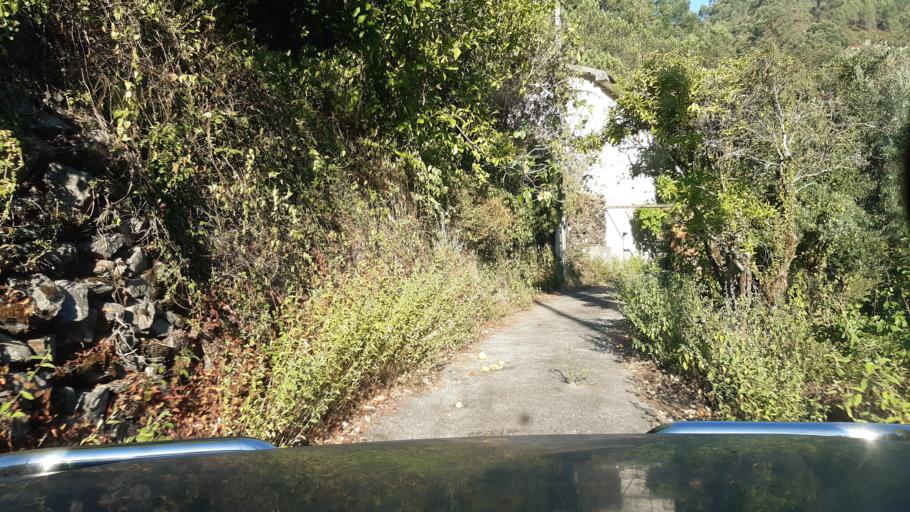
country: PT
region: Viseu
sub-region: Mortagua
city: Mortagua
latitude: 40.5193
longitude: -8.2471
